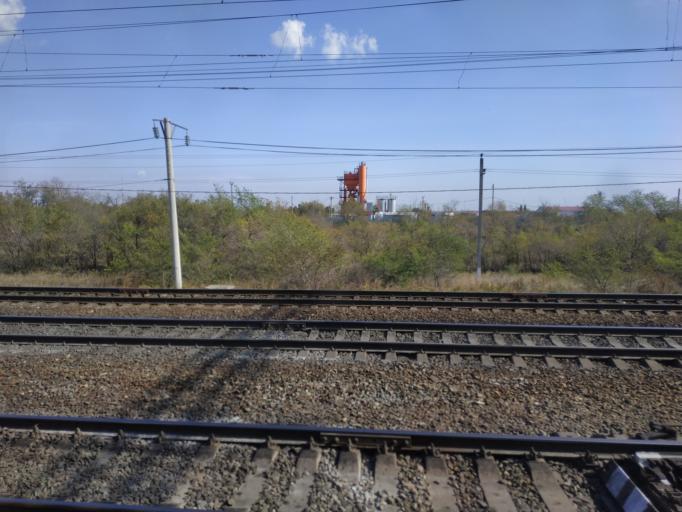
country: RU
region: Volgograd
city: Gumrak
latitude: 48.7920
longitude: 44.3662
